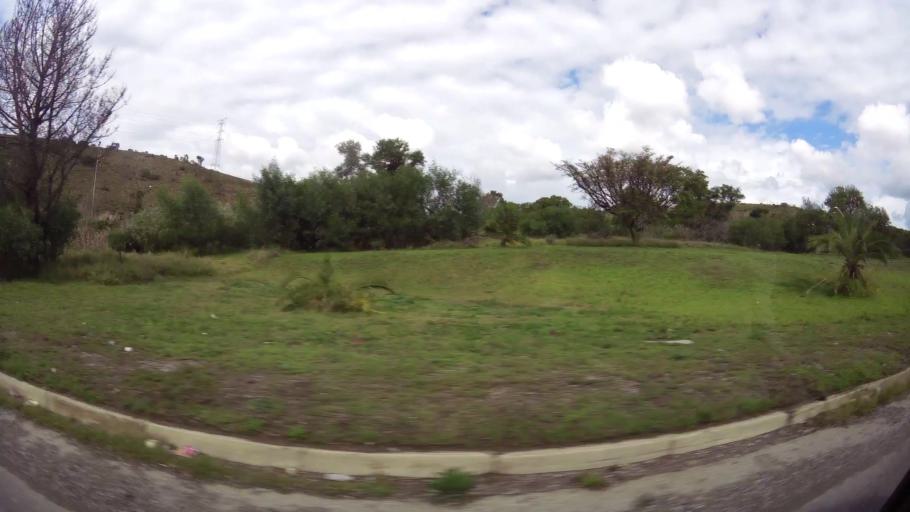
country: ZA
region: Eastern Cape
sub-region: Nelson Mandela Bay Metropolitan Municipality
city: Port Elizabeth
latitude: -33.9300
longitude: 25.5576
